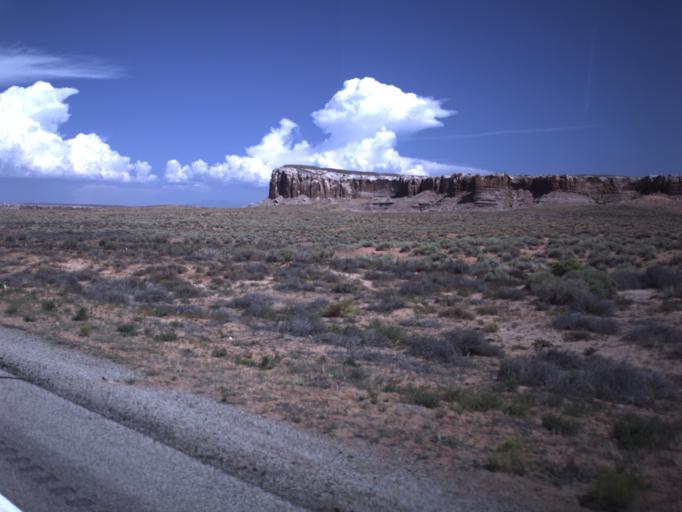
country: US
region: Utah
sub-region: San Juan County
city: Blanding
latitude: 37.2163
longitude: -109.6135
